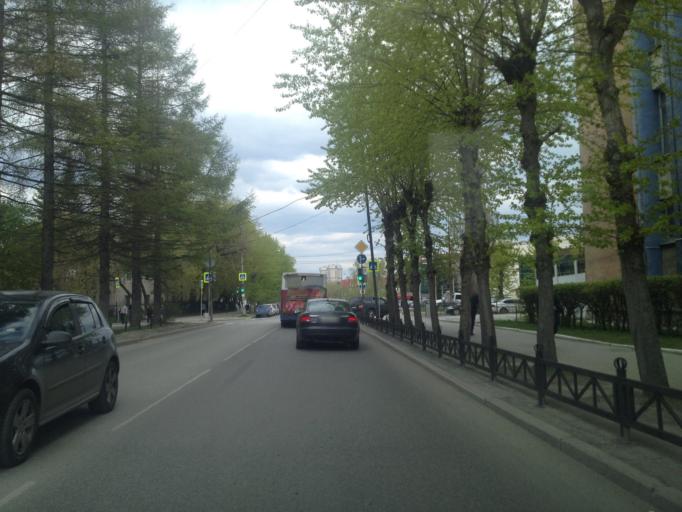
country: RU
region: Sverdlovsk
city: Yekaterinburg
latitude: 56.8529
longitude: 60.6606
